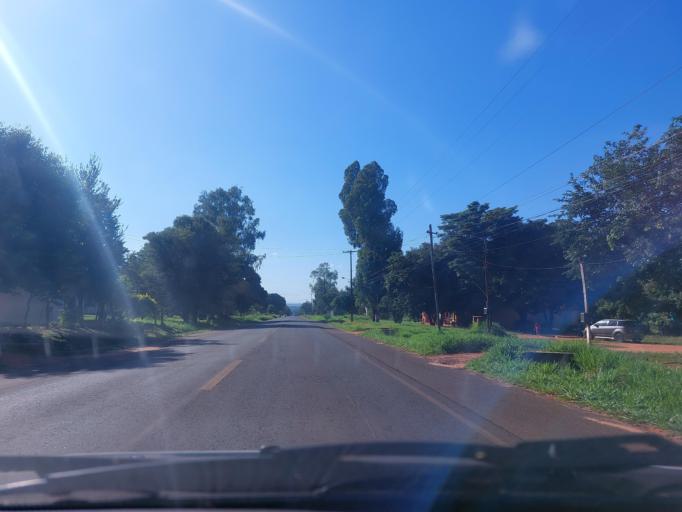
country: PY
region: San Pedro
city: Guayaybi
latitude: -24.5314
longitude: -56.4317
